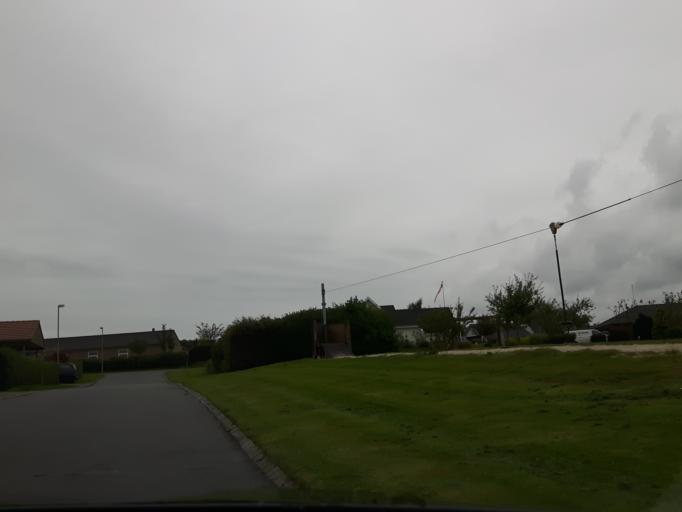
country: DK
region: Central Jutland
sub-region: Skanderborg Kommune
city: Ry
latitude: 56.1552
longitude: 9.8043
